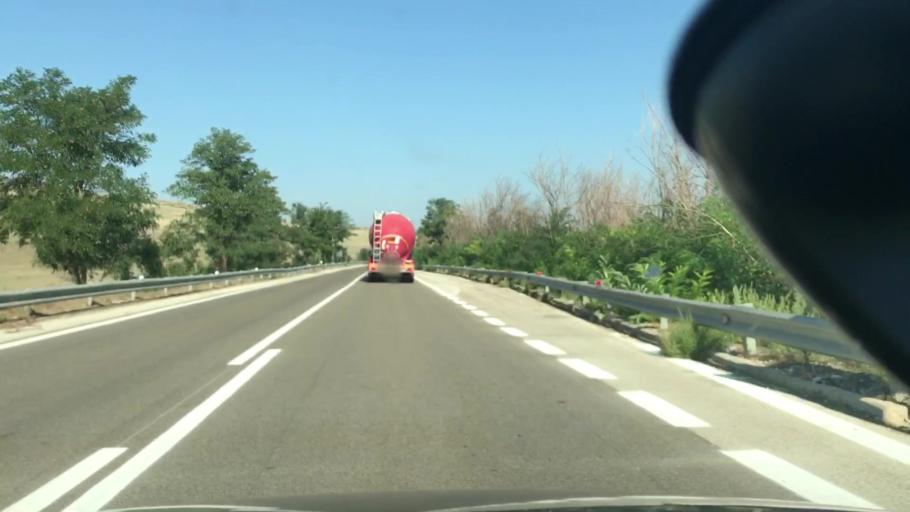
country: IT
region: Basilicate
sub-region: Provincia di Matera
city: Irsina
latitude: 40.7931
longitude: 16.2797
